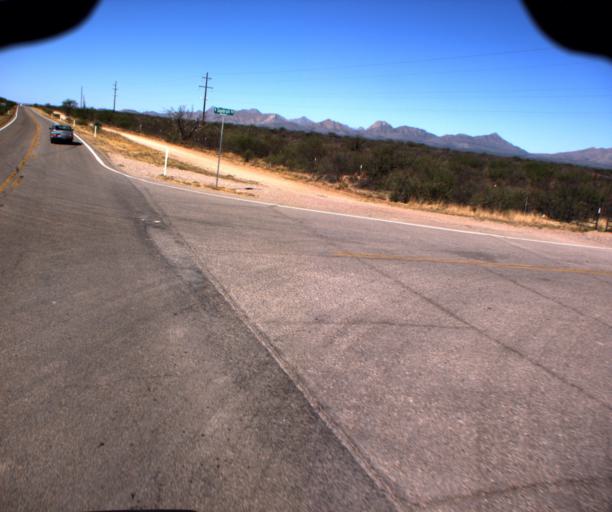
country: US
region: Arizona
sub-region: Cochise County
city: Huachuca City
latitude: 31.7079
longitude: -110.2822
